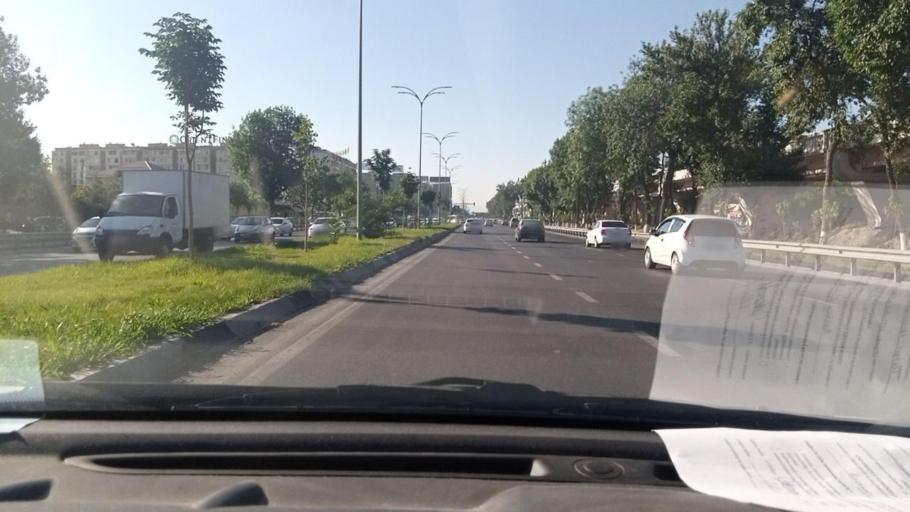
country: UZ
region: Toshkent
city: Salor
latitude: 41.2946
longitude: 69.3542
